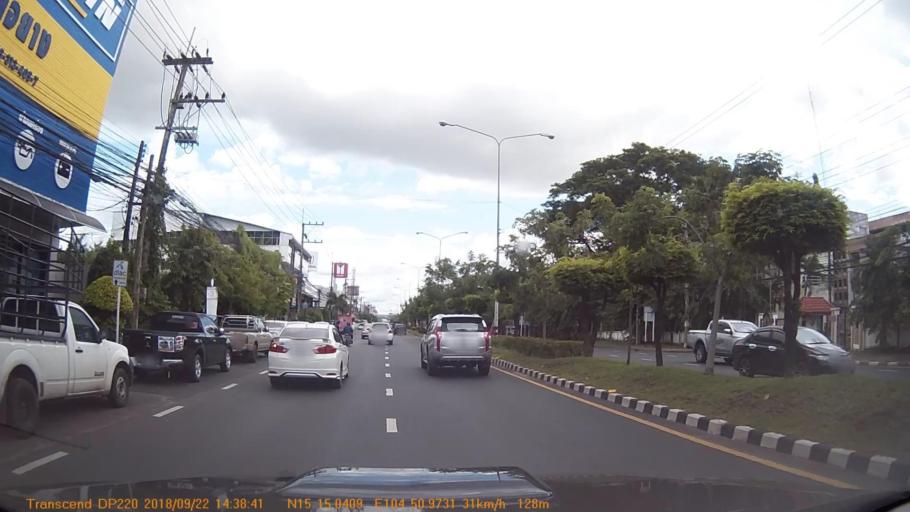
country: TH
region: Changwat Ubon Ratchathani
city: Ubon Ratchathani
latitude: 15.2503
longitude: 104.8497
